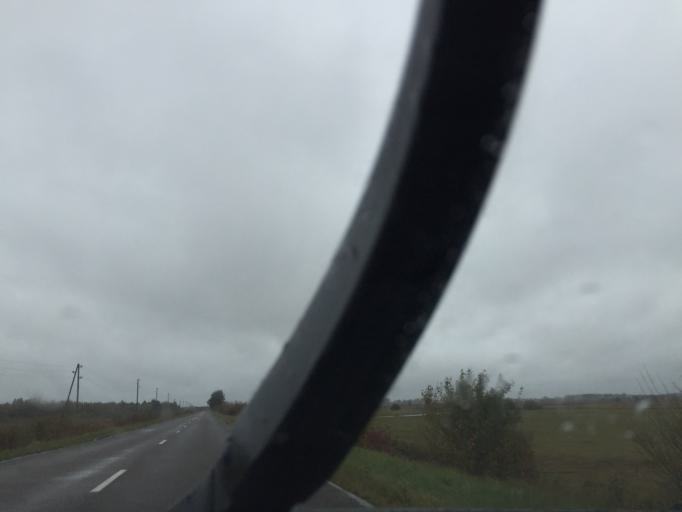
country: LV
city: Tireli
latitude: 56.8163
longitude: 23.5712
